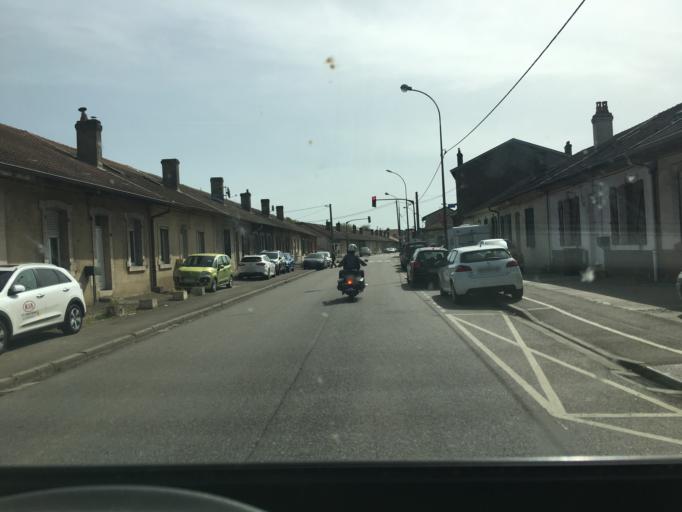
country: FR
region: Lorraine
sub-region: Departement de Meurthe-et-Moselle
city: Neuves-Maisons
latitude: 48.6143
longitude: 6.1154
